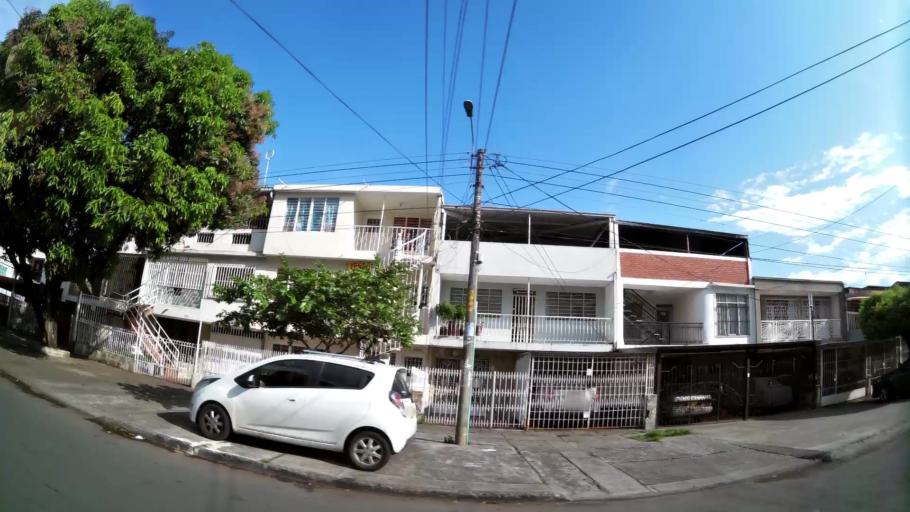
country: CO
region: Valle del Cauca
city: Cali
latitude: 3.4297
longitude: -76.5266
